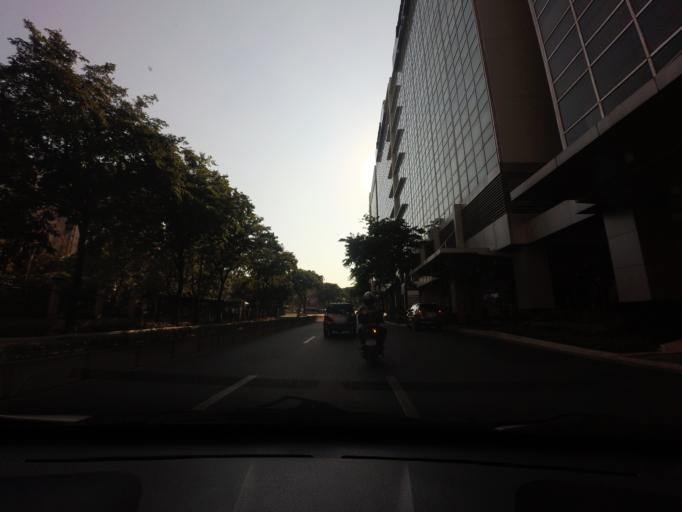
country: PH
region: Metro Manila
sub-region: Makati City
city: Makati City
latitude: 14.5352
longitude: 121.0497
